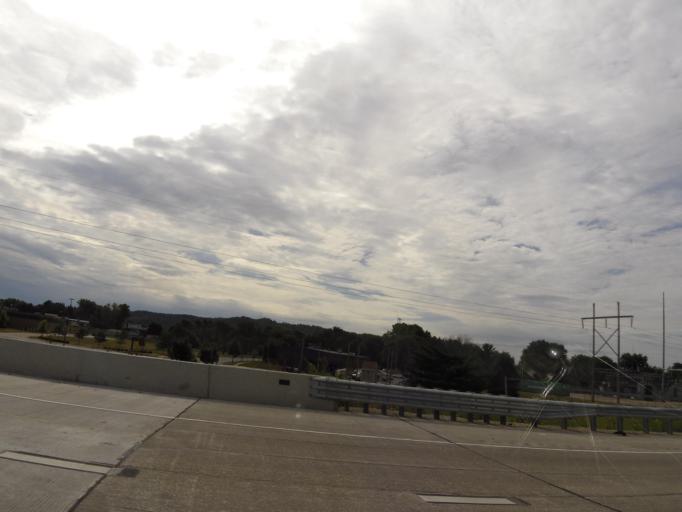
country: US
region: Wisconsin
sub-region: La Crosse County
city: Onalaska
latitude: 43.8704
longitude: -91.2186
